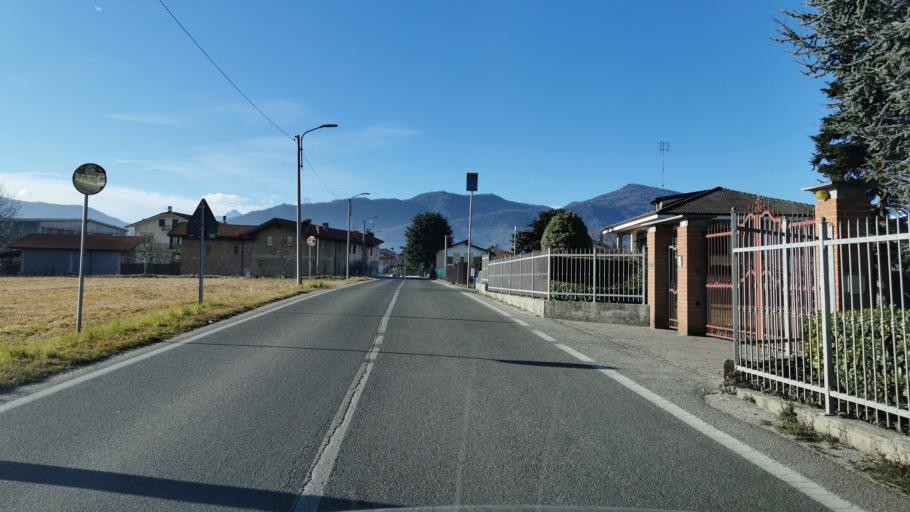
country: IT
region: Piedmont
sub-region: Provincia di Cuneo
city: Caraglio
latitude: 44.4216
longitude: 7.4375
